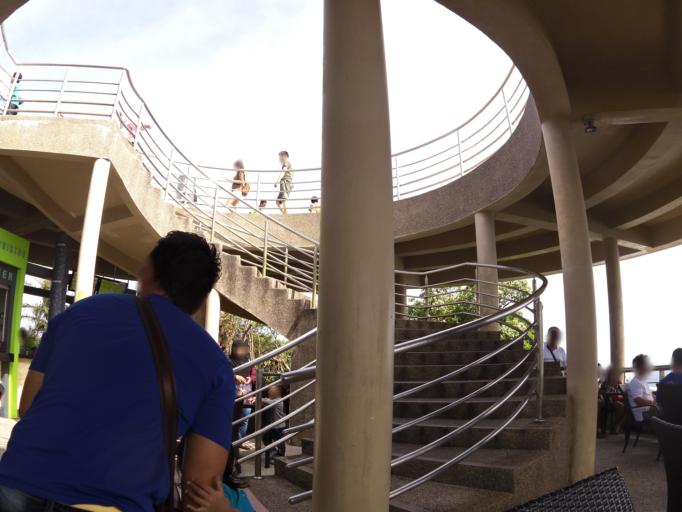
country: MY
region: Kedah
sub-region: Langkawi
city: Kuah
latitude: 6.3851
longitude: 99.6610
